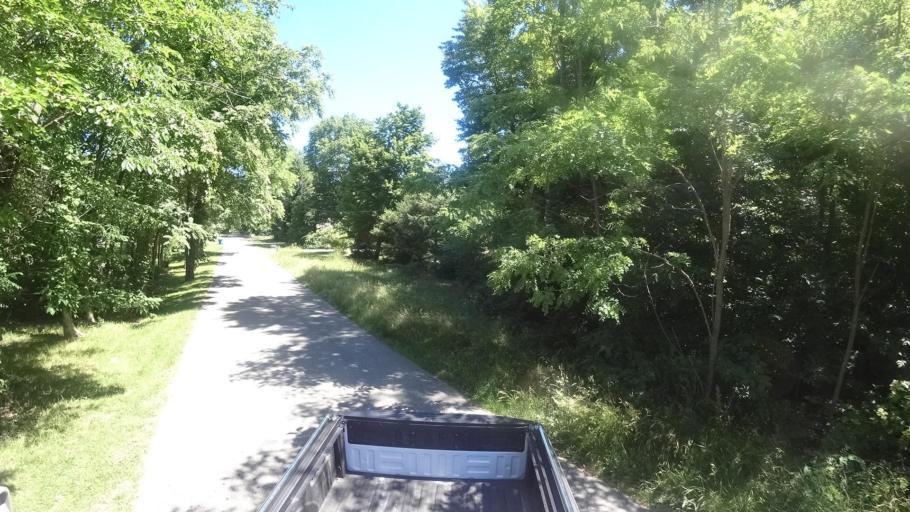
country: US
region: Indiana
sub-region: Porter County
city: Porter
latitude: 41.6386
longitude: -87.0578
